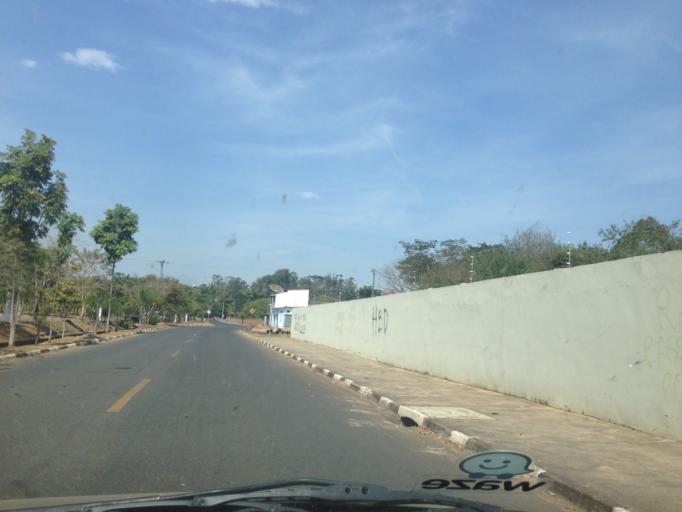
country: BR
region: Sao Paulo
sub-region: Casa Branca
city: Casa Branca
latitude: -21.7782
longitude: -47.0897
